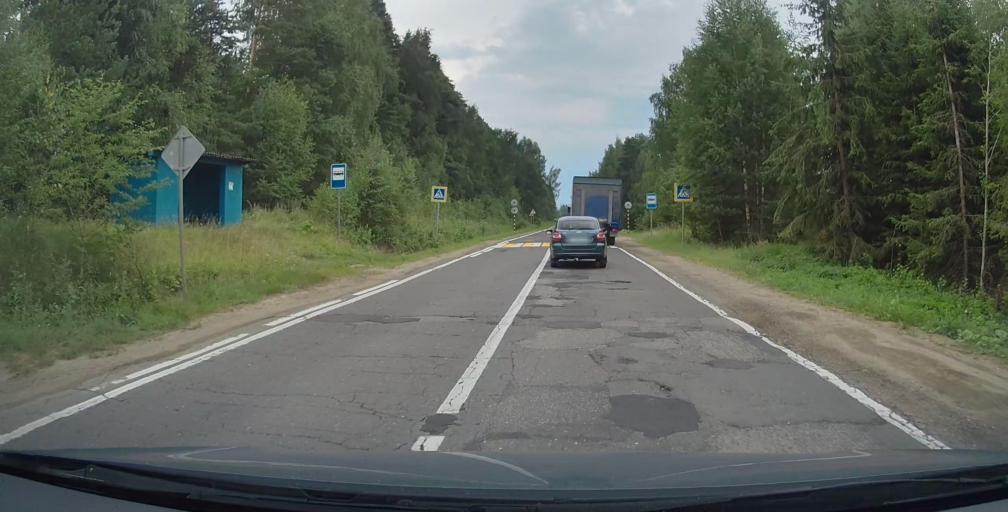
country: RU
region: Jaroslavl
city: Myshkin
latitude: 57.8541
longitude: 38.5104
